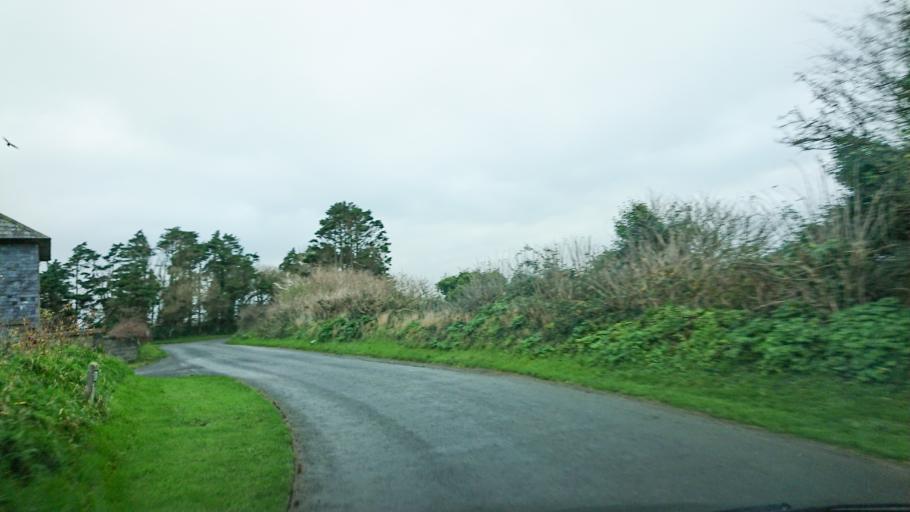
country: IE
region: Munster
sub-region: Waterford
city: Dunmore East
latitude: 52.2054
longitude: -6.9882
